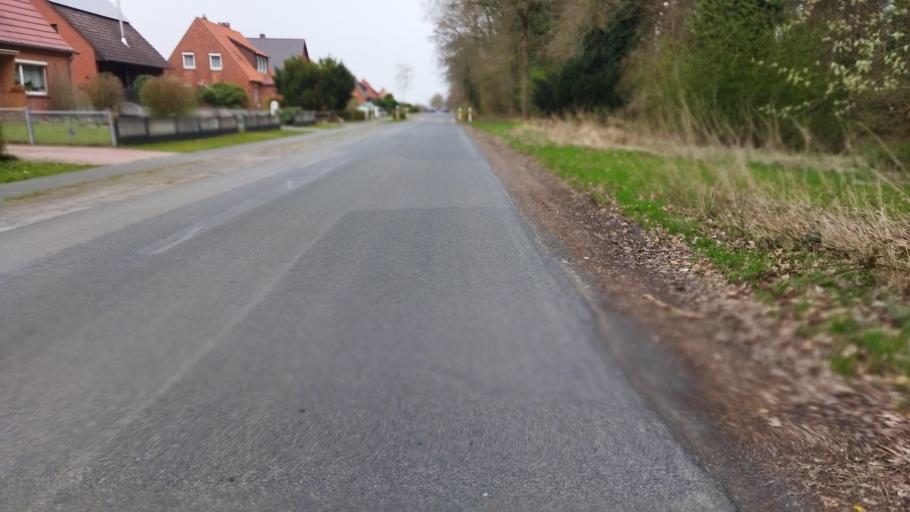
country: DE
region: Lower Saxony
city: Estorf
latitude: 52.5969
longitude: 9.1620
